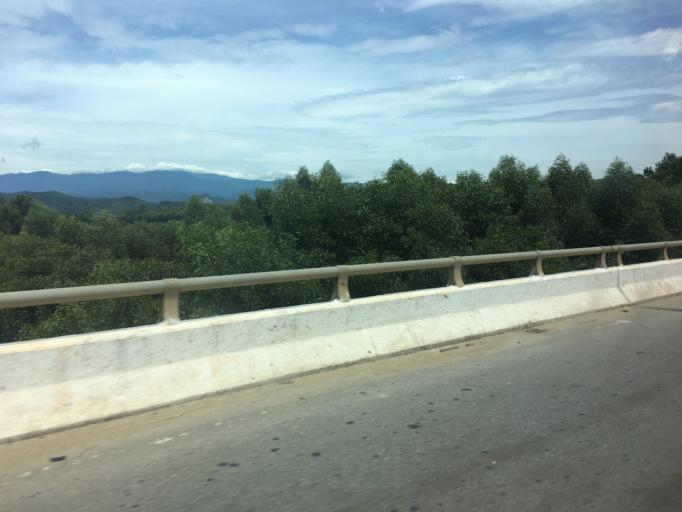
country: VN
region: Ha Tinh
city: Huong Khe
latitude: 18.2740
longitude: 105.6289
